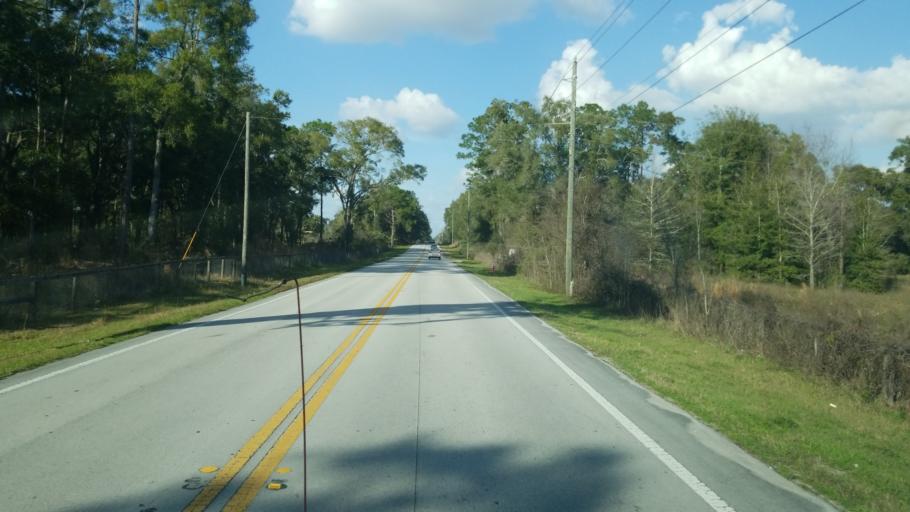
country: US
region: Florida
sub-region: Marion County
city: Ocala
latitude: 29.1602
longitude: -82.2519
